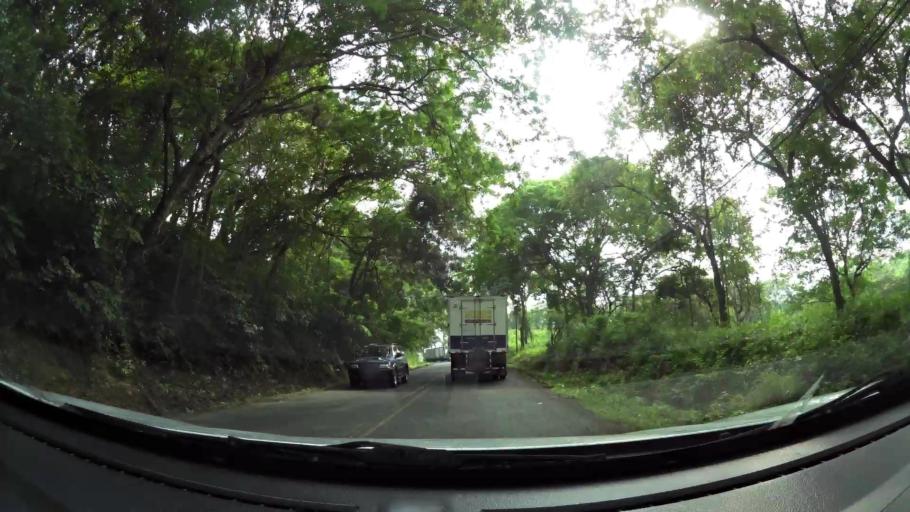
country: CR
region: Guanacaste
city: Juntas
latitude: 10.1877
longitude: -84.9459
